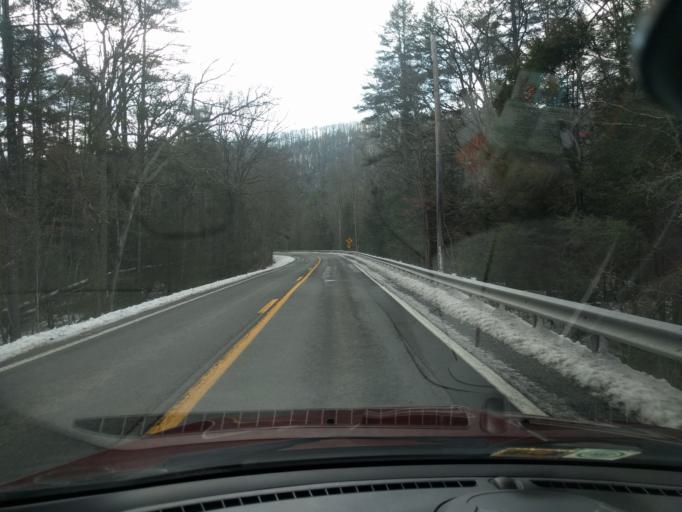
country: US
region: West Virginia
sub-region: Pocahontas County
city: Marlinton
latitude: 38.1385
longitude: -79.9742
